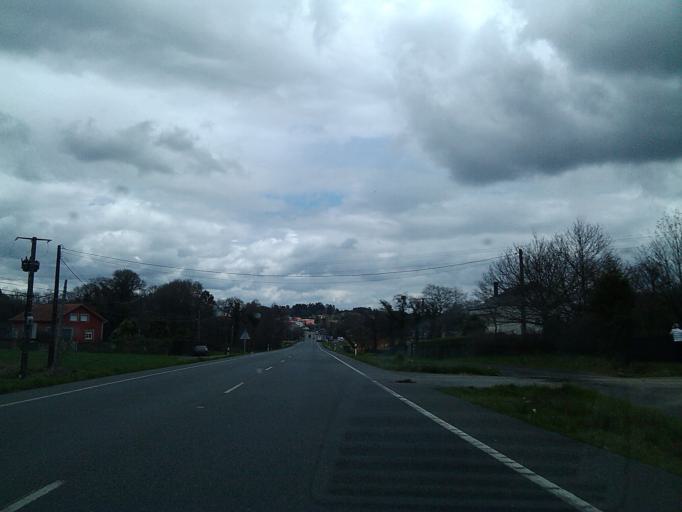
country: ES
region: Galicia
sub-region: Provincia da Coruna
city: Curtis
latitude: 43.1314
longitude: -8.0439
